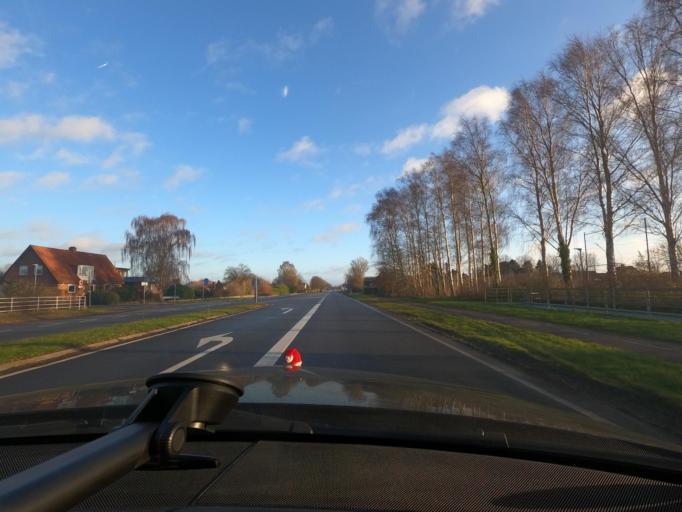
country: DK
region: South Denmark
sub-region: Sonderborg Kommune
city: Grasten
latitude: 54.9045
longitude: 9.6170
